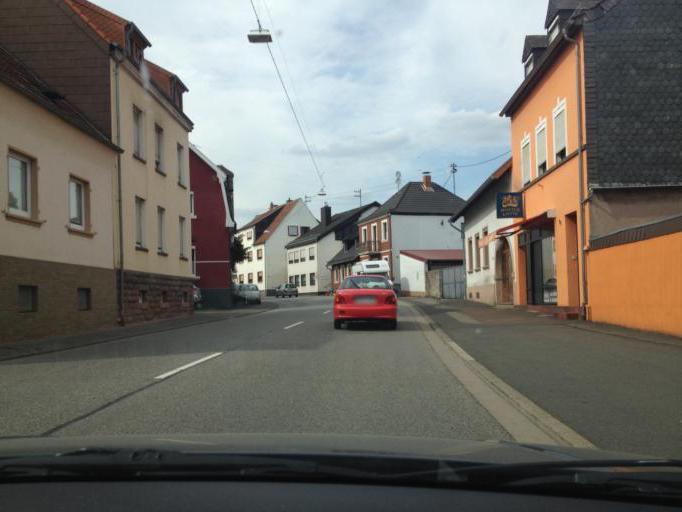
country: DE
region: Saarland
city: Sankt Wendel
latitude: 49.4707
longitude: 7.1629
